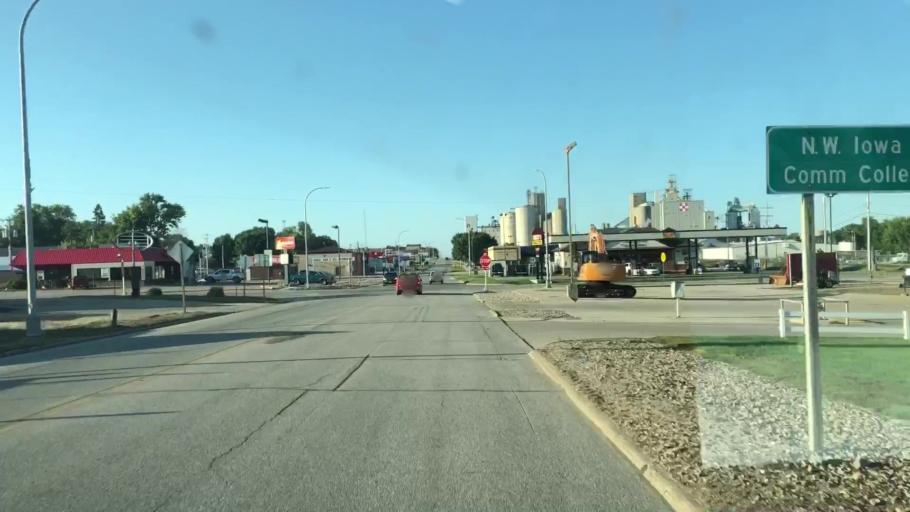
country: US
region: Iowa
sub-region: O'Brien County
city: Sheldon
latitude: 43.1866
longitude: -95.8540
